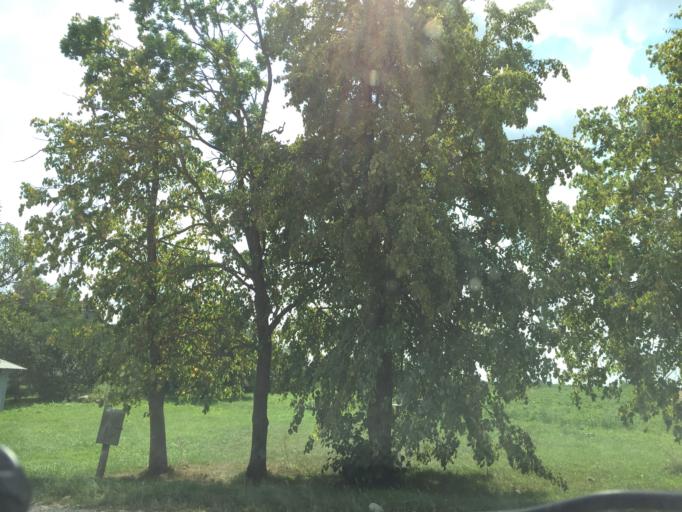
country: LT
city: Zagare
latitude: 56.3354
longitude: 23.0795
